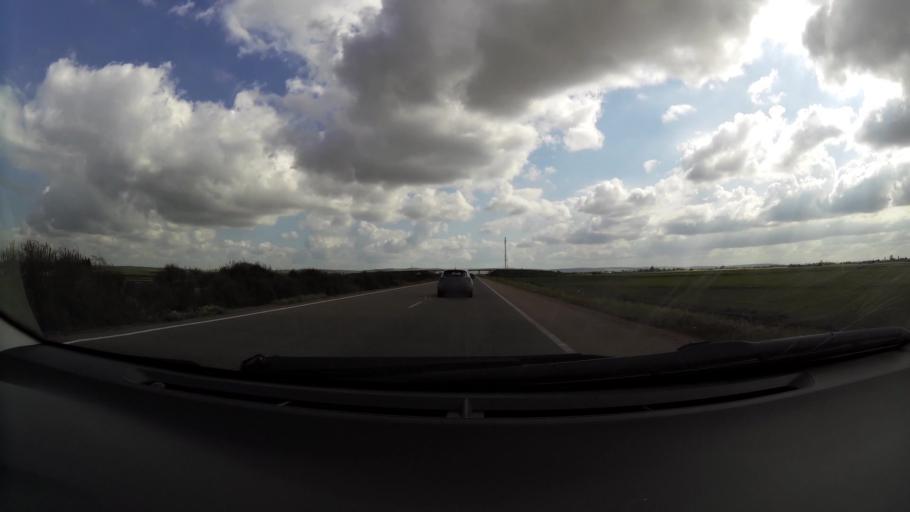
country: MA
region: Chaouia-Ouardigha
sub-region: Settat Province
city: Berrechid
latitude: 33.1396
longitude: -7.5759
